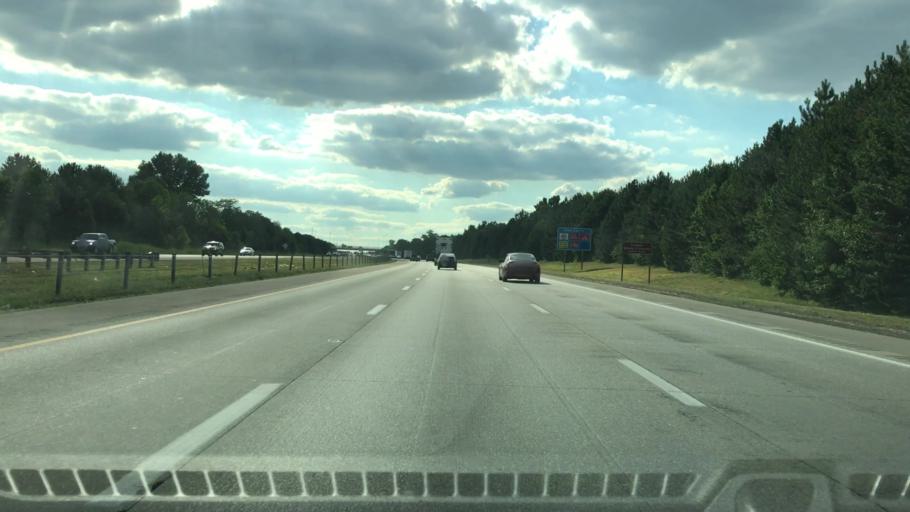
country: US
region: Ohio
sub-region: Franklin County
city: Grove City
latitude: 39.8998
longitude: -83.0547
